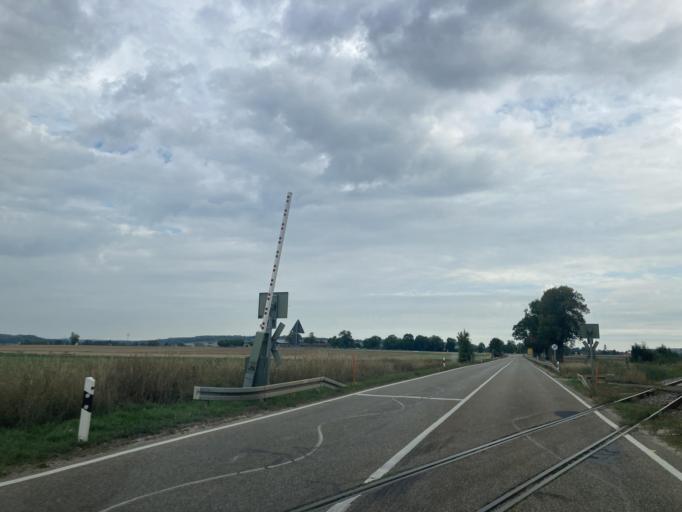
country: DE
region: Bavaria
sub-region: Swabia
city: Munningen
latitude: 48.9350
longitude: 10.5852
